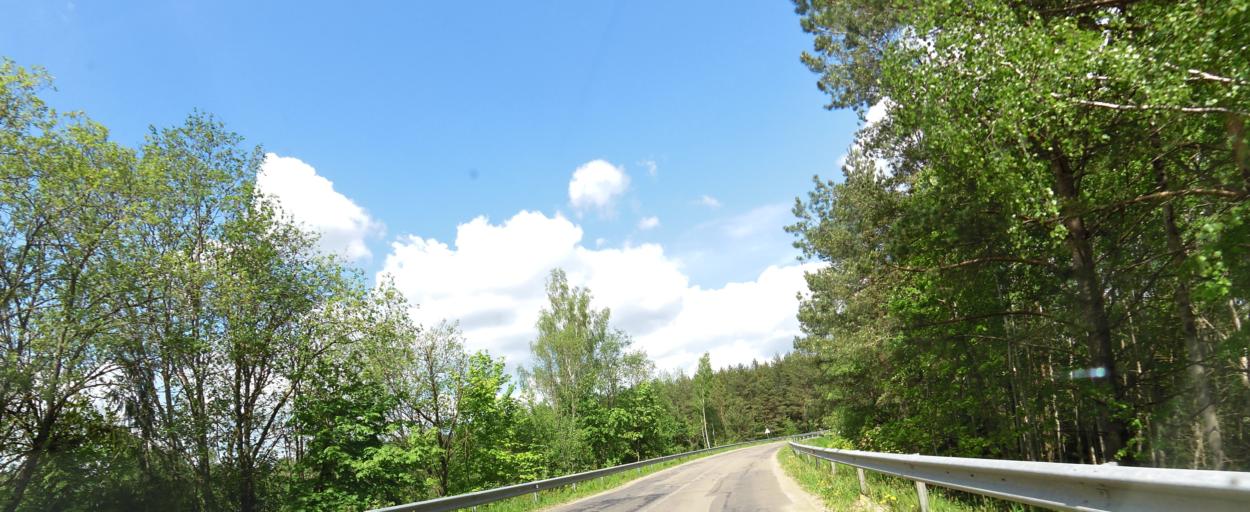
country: LT
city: Trakai
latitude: 54.7136
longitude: 24.9733
